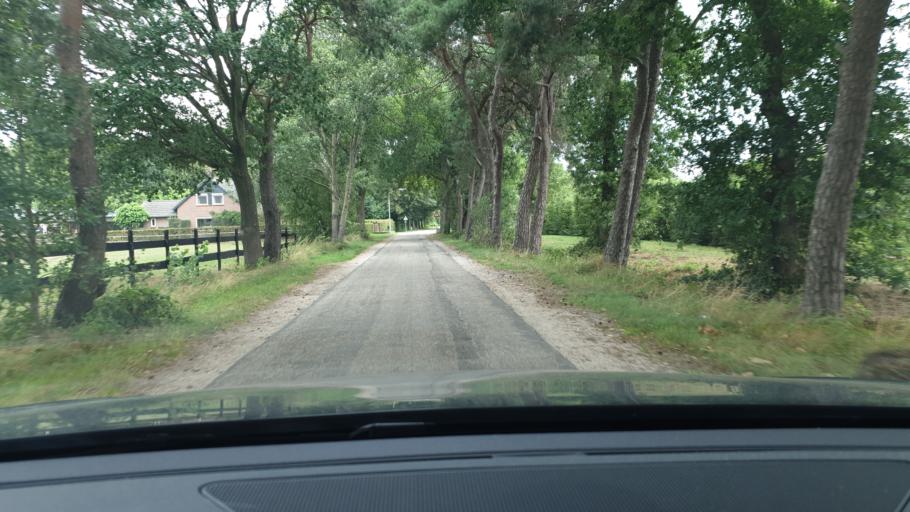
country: NL
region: North Brabant
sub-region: Gemeente Best
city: Best
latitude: 51.5010
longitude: 5.3633
